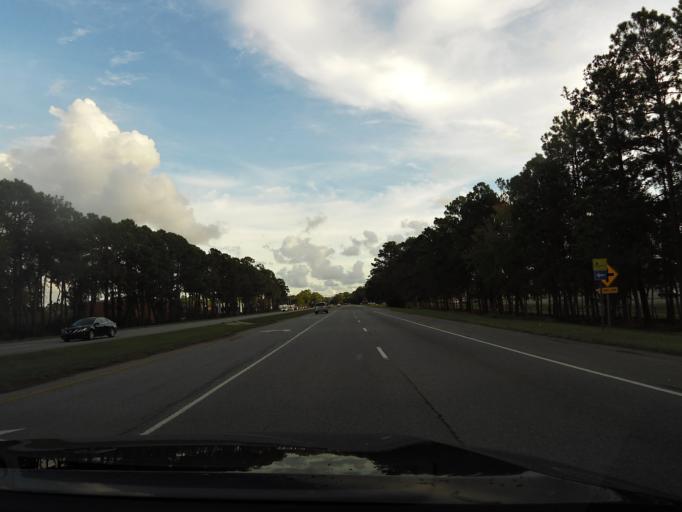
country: US
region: Georgia
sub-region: Glynn County
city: Country Club Estates
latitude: 31.2155
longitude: -81.4917
